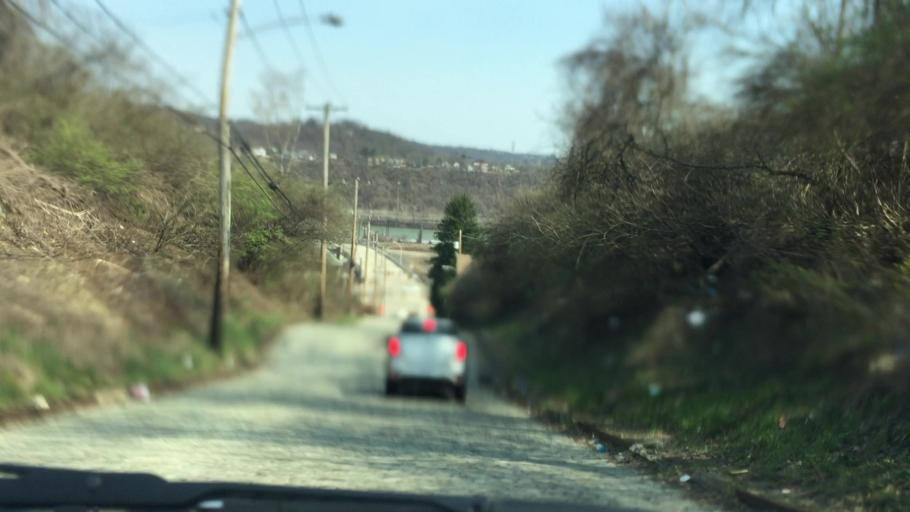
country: US
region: Pennsylvania
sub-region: Allegheny County
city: West Mifflin
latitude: 40.3648
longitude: -79.8454
